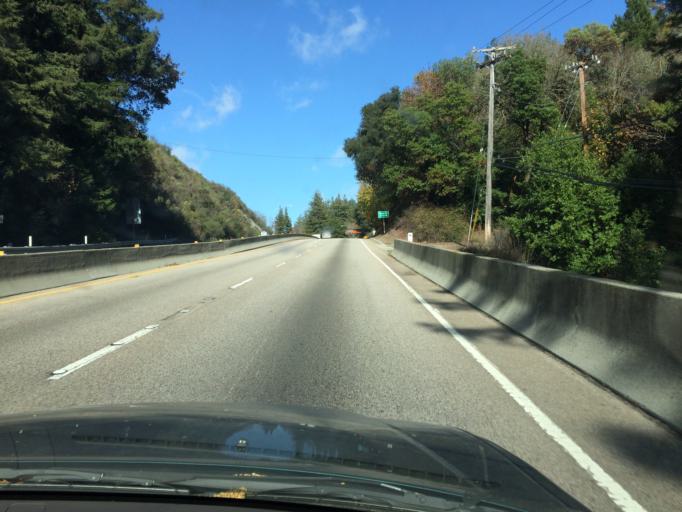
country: US
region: California
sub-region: Santa Clara County
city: Lexington Hills
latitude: 37.1426
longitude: -121.9851
